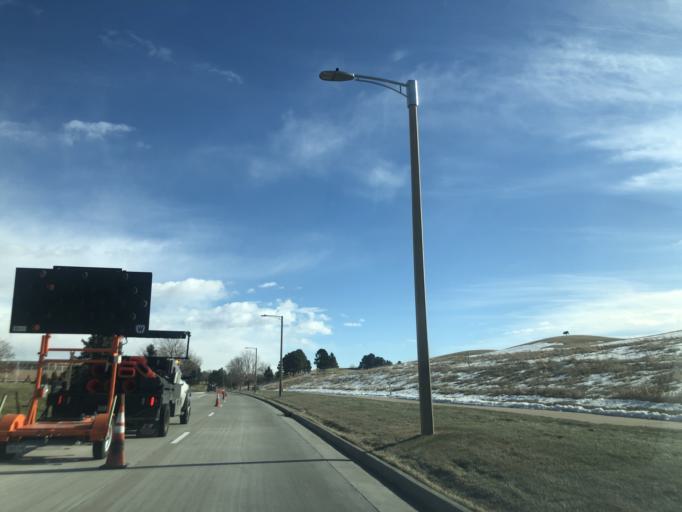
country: US
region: Colorado
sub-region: Douglas County
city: Meridian
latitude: 39.5482
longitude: -104.8497
